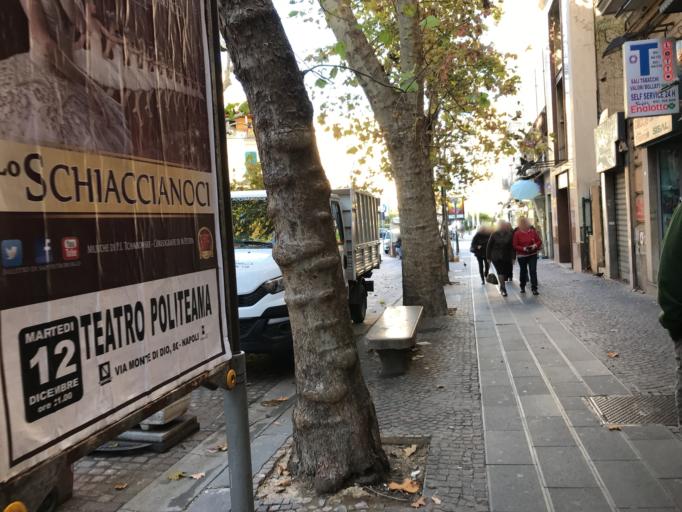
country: IT
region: Campania
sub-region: Provincia di Napoli
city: Napoli
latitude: 40.8471
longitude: 14.2280
